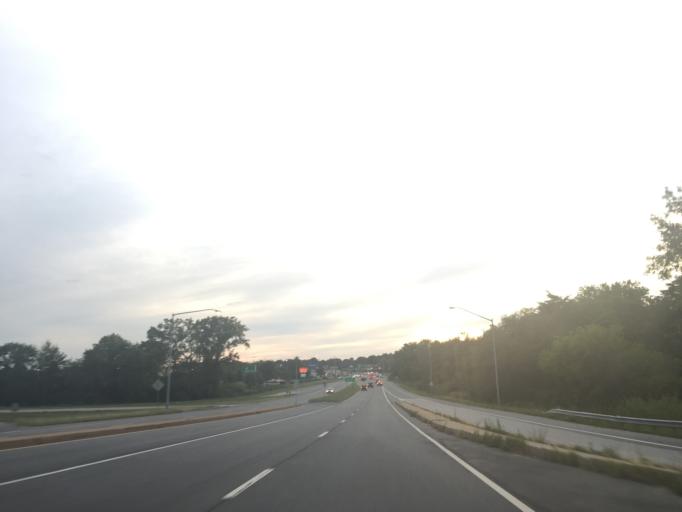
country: US
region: Maryland
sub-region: Anne Arundel County
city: Brooklyn Park
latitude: 39.1939
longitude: -76.6044
